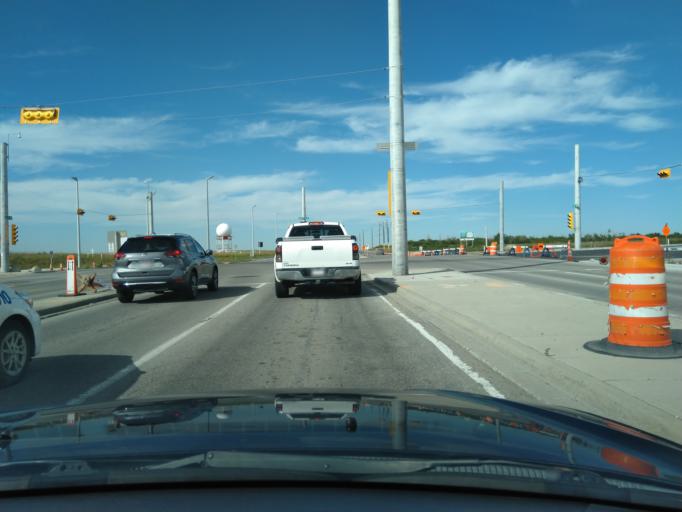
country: CA
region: Alberta
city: Calgary
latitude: 51.1393
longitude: -113.9817
